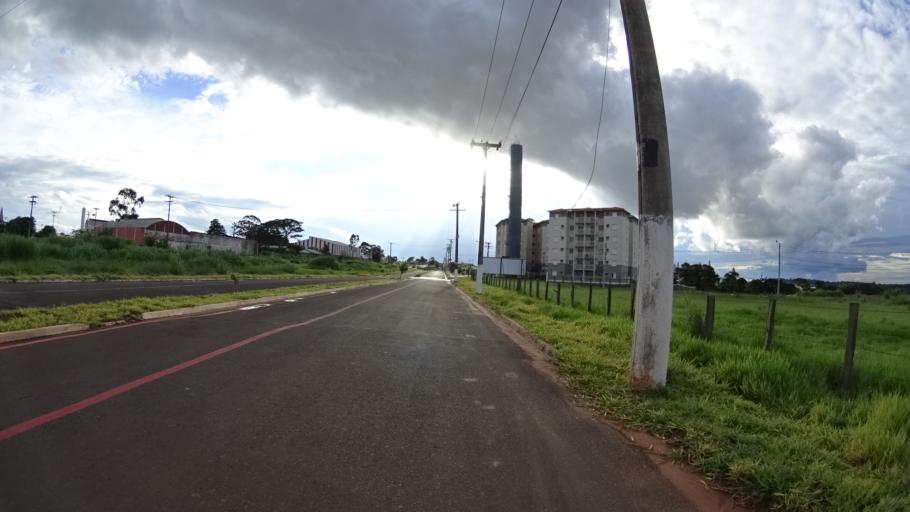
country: BR
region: Sao Paulo
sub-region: Marilia
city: Marilia
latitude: -22.2256
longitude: -49.9014
